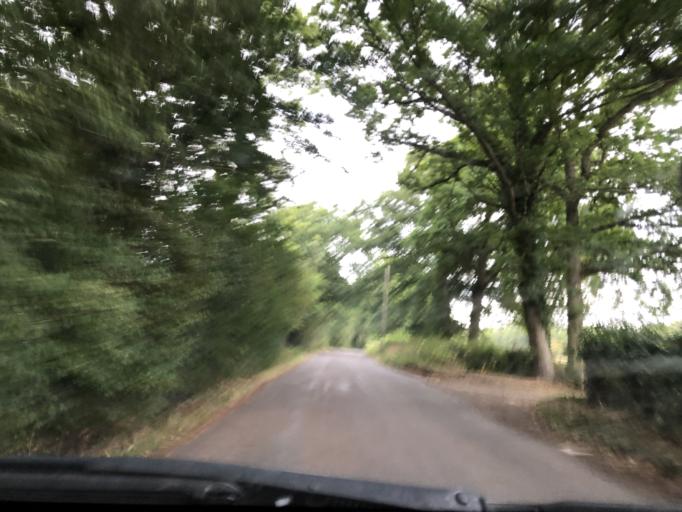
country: GB
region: England
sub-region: Kent
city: Tonbridge
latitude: 51.2314
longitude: 0.2361
